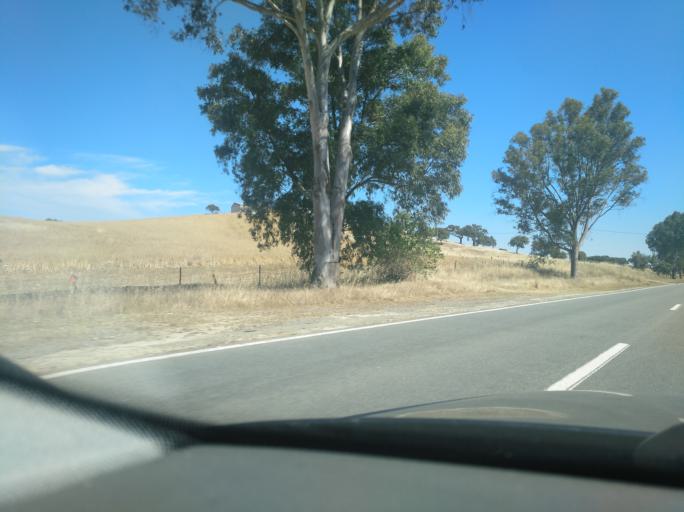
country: PT
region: Beja
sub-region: Castro Verde
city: Castro Verde
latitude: 37.6759
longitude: -8.0826
